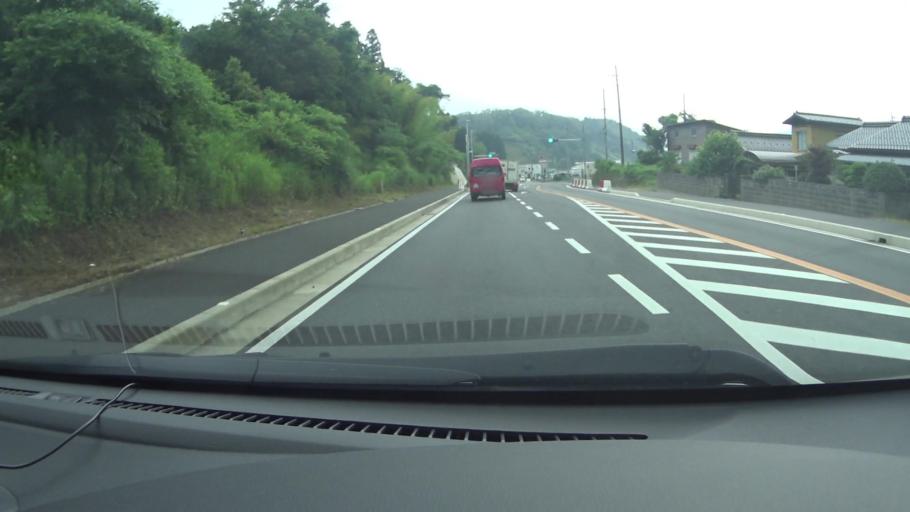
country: JP
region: Kyoto
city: Ayabe
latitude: 35.3082
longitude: 135.2757
